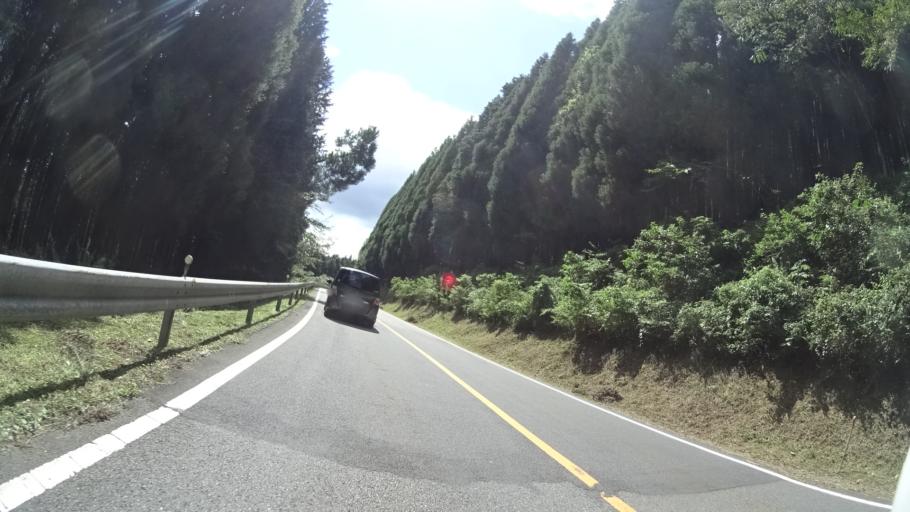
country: JP
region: Oita
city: Tsukawaki
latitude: 33.2217
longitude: 131.2982
